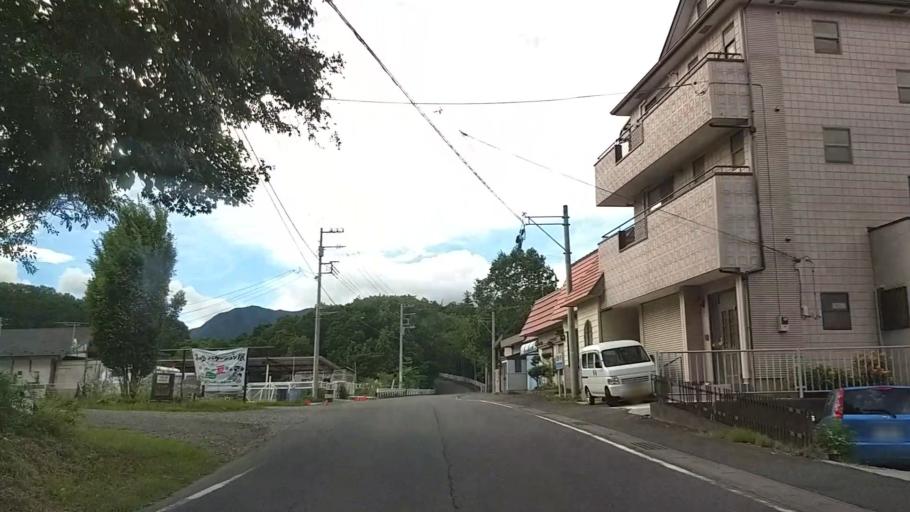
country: JP
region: Yamanashi
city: Uenohara
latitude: 35.5897
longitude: 139.1505
